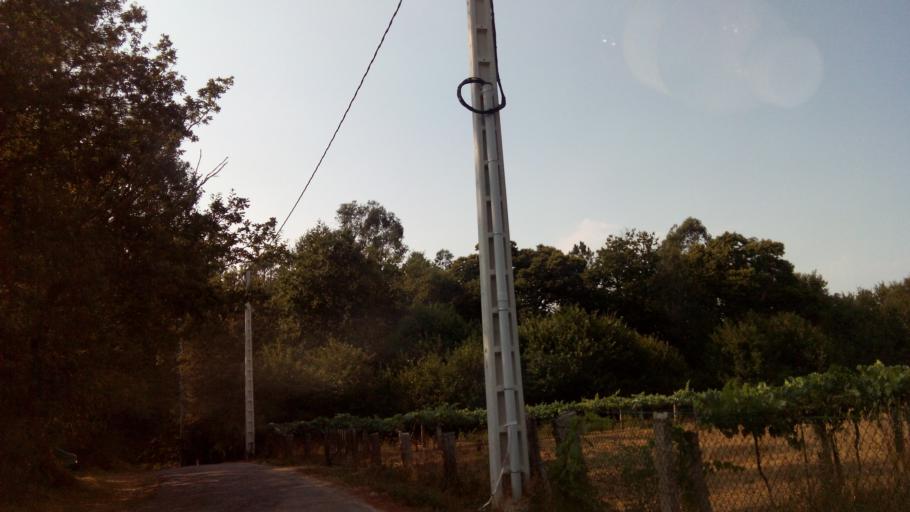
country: ES
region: Galicia
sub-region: Provincia de Pontevedra
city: Ponteareas
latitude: 42.1868
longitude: -8.5104
